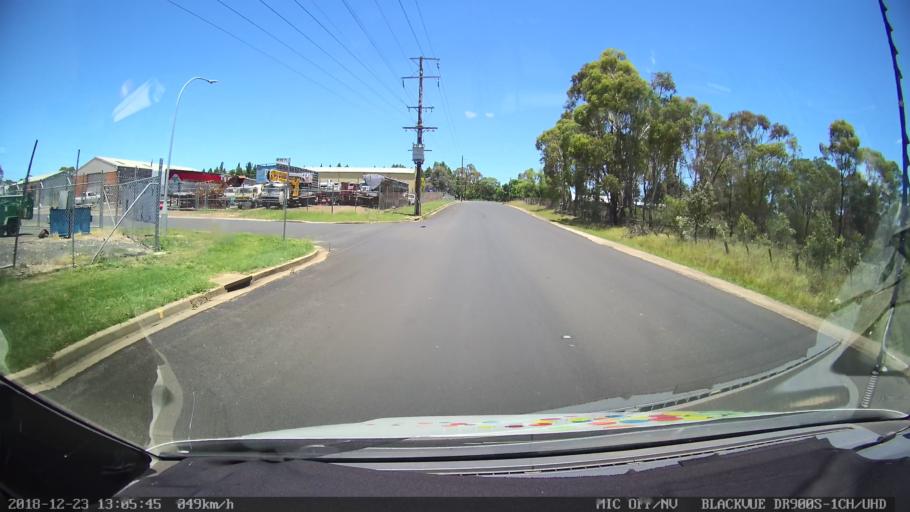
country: AU
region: New South Wales
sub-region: Armidale Dumaresq
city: Armidale
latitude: -30.5155
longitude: 151.6410
